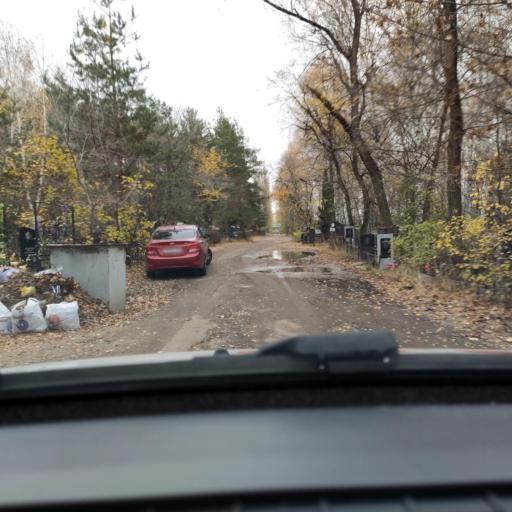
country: RU
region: Voronezj
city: Pridonskoy
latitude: 51.6707
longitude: 39.1137
